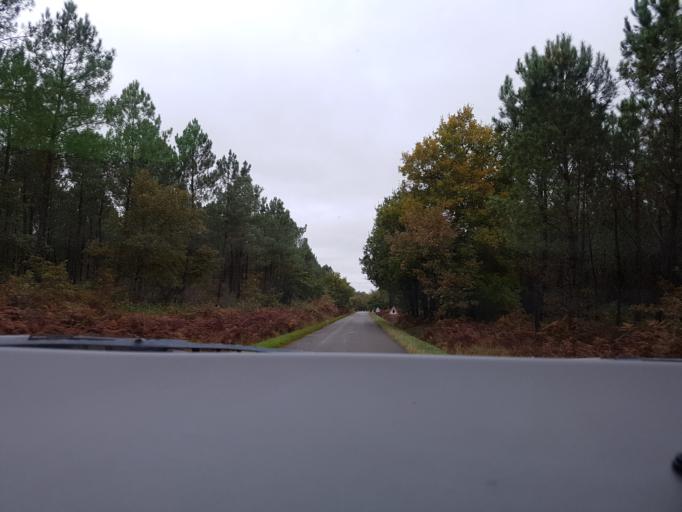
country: FR
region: Aquitaine
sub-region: Departement des Landes
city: Roquefort
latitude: 44.0639
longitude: -0.3541
